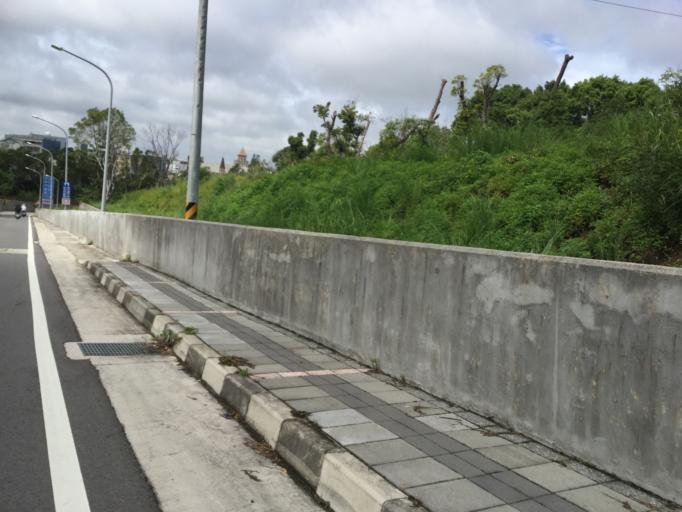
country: TW
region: Taiwan
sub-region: Hsinchu
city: Hsinchu
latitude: 24.7804
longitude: 121.0152
